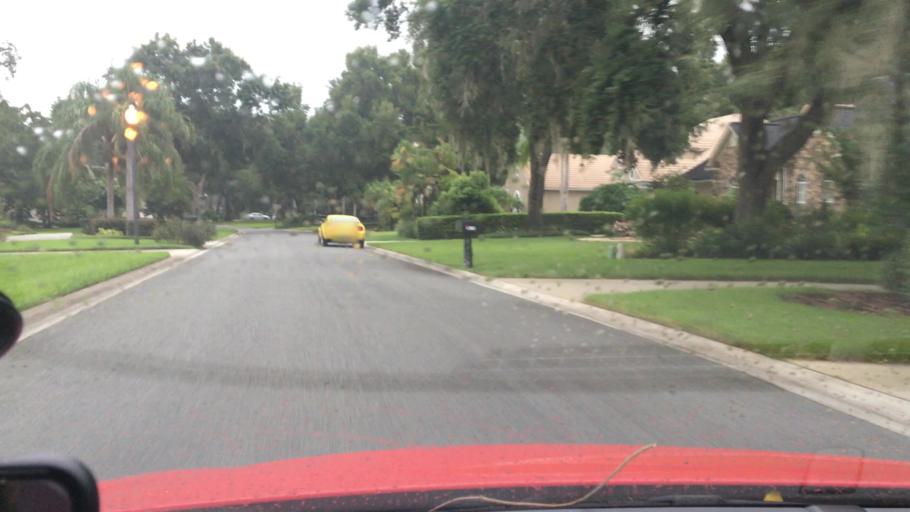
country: US
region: Florida
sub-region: Lake County
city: Mount Dora
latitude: 28.8457
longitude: -81.6380
